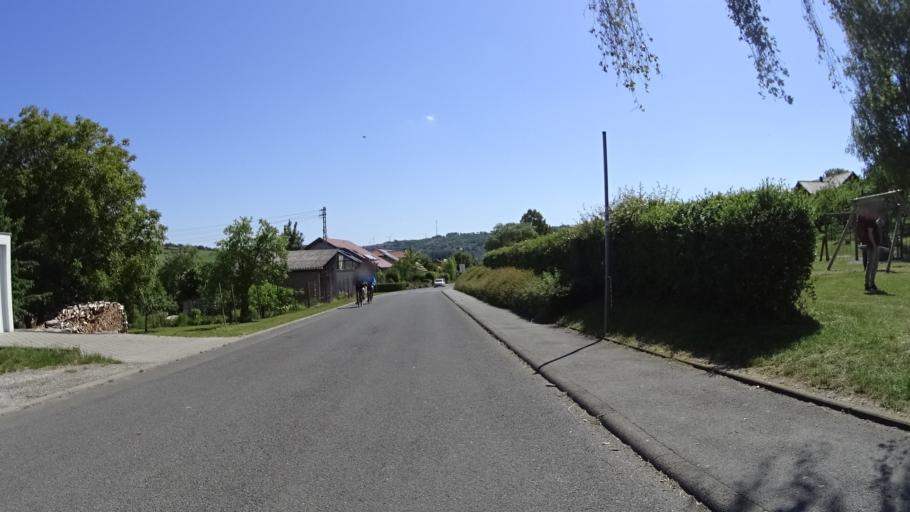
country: DE
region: Baden-Wuerttemberg
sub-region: Regierungsbezirk Stuttgart
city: Weikersheim
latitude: 49.4685
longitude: 9.8737
